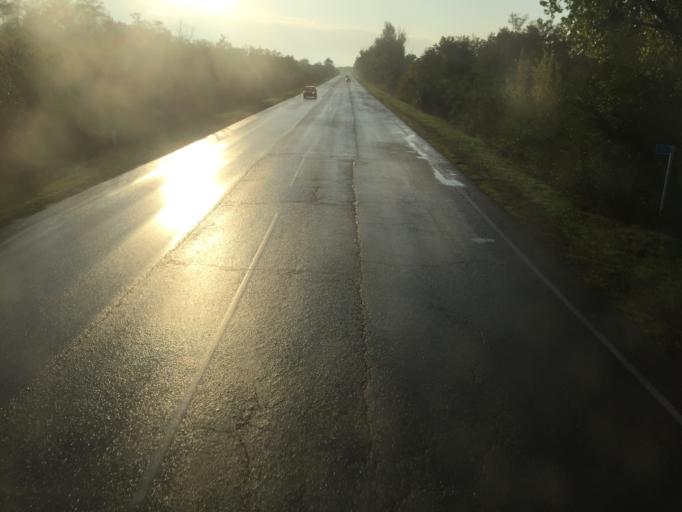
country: RU
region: Rostov
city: Kirovskaya
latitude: 47.0214
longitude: 39.8976
